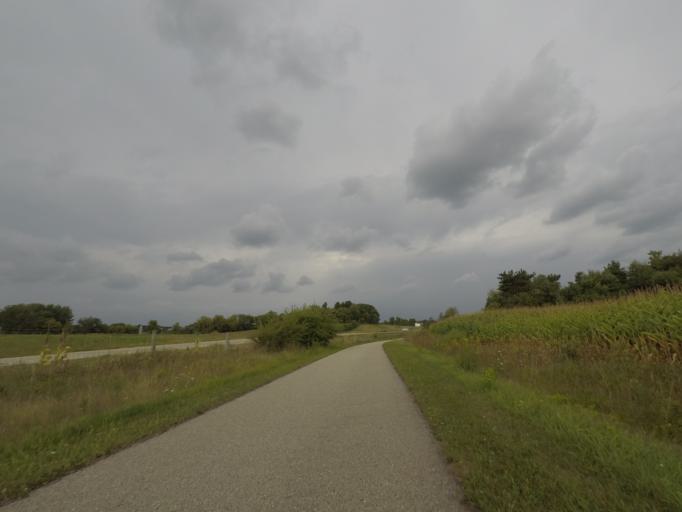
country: US
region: Wisconsin
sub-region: Jefferson County
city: Jefferson
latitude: 42.9786
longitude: -88.8230
